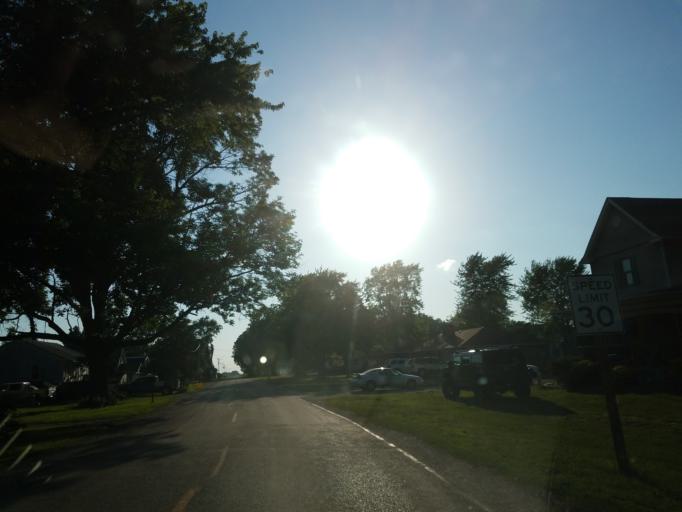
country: US
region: Illinois
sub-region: McLean County
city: Twin Grove
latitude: 40.4073
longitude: -89.0625
